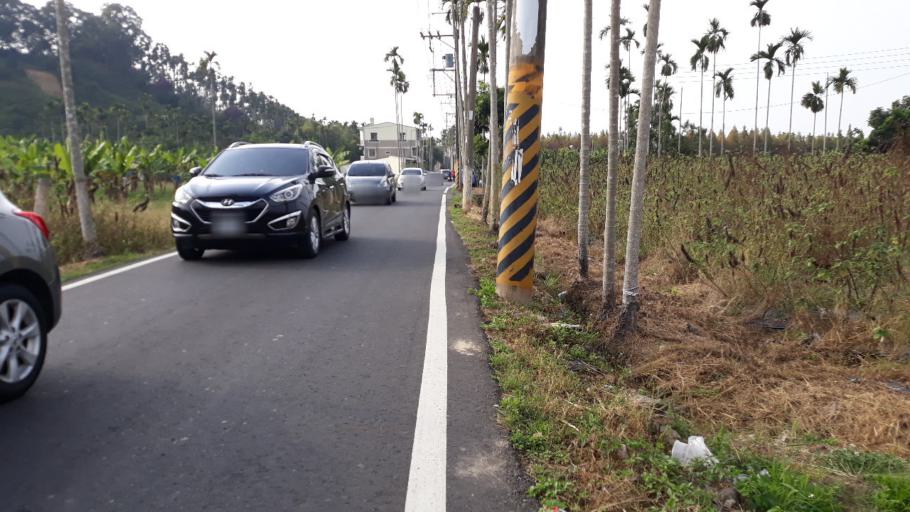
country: TW
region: Taiwan
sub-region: Chiayi
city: Jiayi Shi
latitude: 23.4303
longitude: 120.5202
